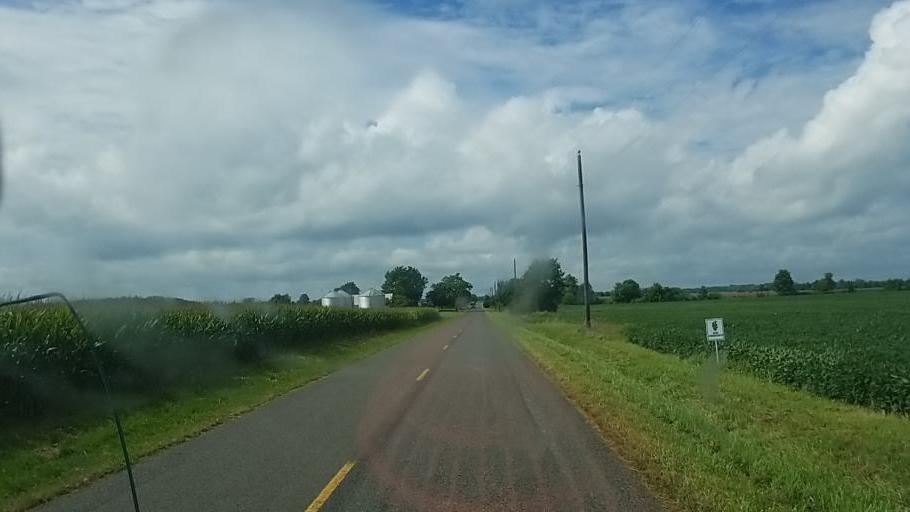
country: US
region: Ohio
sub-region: Hardin County
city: Kenton
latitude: 40.4812
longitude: -83.5124
